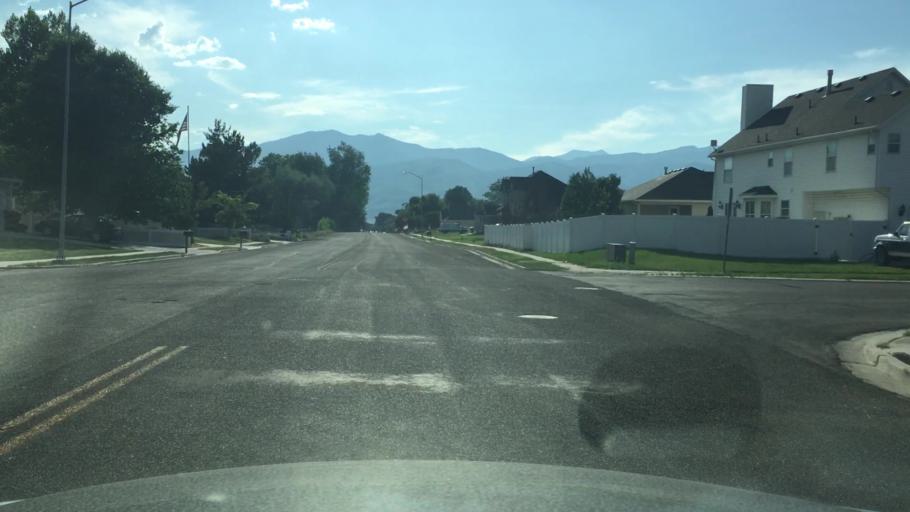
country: US
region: Utah
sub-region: Wasatch County
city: Heber
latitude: 40.5002
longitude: -111.4016
